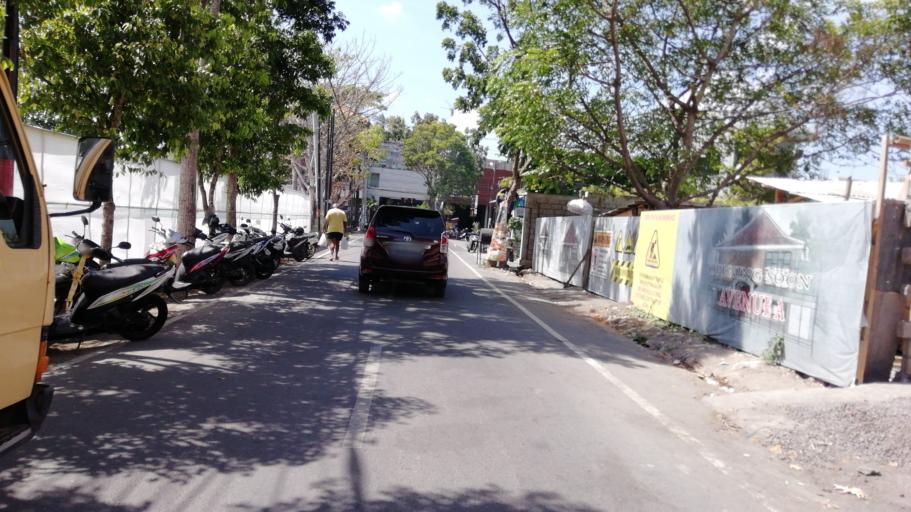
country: ID
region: Bali
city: Banjar Kerobokan
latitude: -8.6596
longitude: 115.1392
